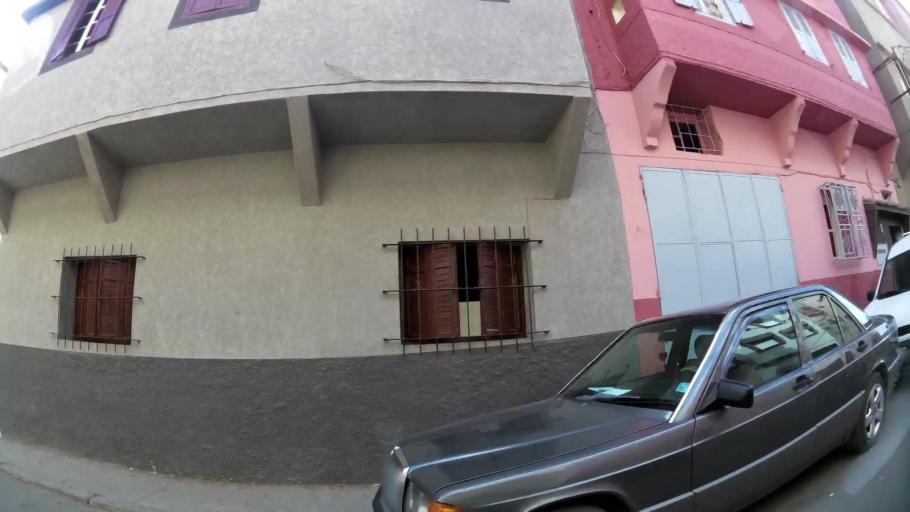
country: MA
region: Gharb-Chrarda-Beni Hssen
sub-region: Kenitra Province
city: Kenitra
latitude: 34.2620
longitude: -6.5607
